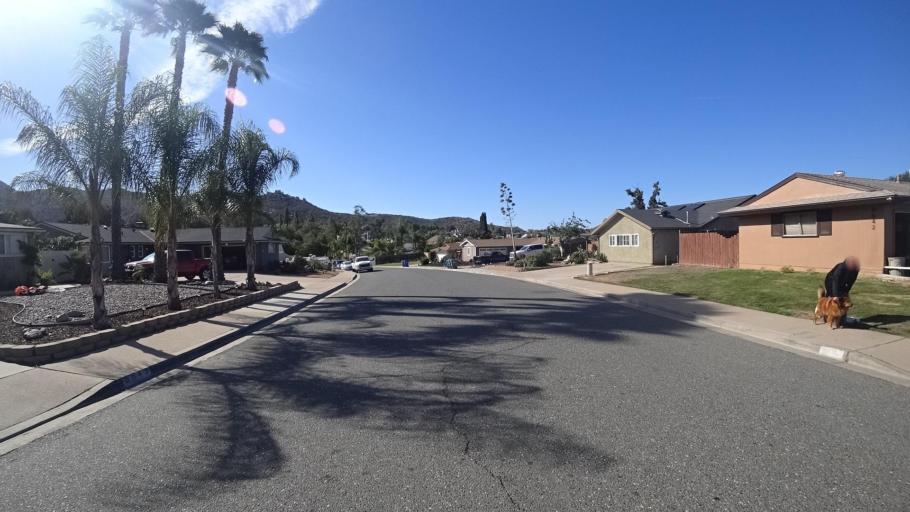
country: US
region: California
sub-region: San Diego County
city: Granite Hills
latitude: 32.8334
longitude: -116.8983
